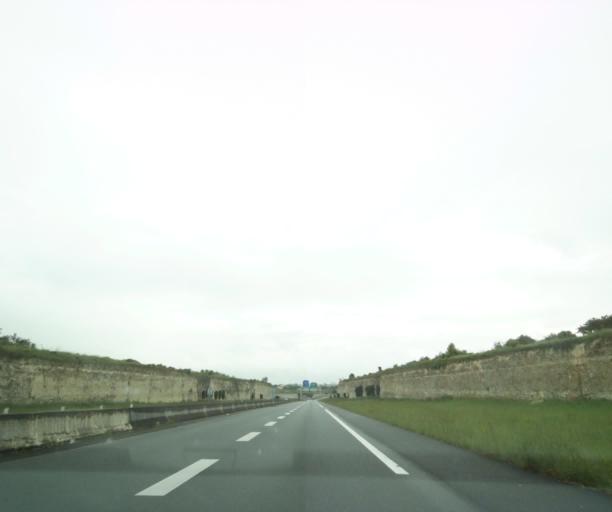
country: FR
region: Poitou-Charentes
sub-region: Departement de la Charente-Maritime
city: Saintes
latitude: 45.7222
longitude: -0.6530
